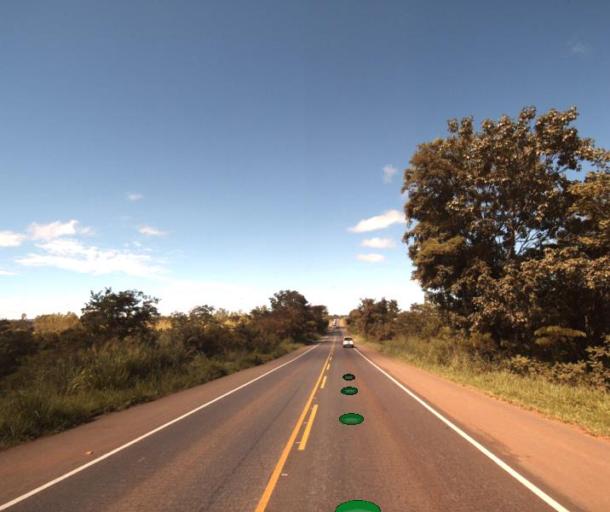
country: BR
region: Goias
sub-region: Rialma
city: Rialma
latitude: -15.2915
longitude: -49.5683
